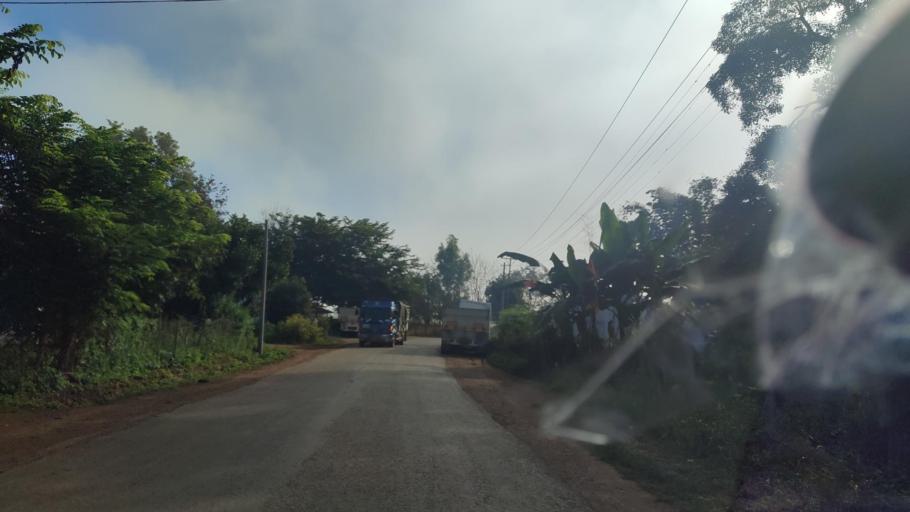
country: MM
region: Shan
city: Taunggyi
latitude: 20.9281
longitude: 97.6605
